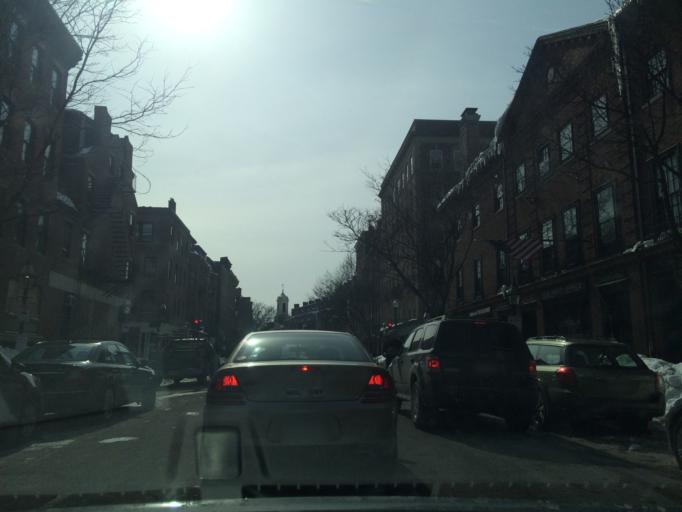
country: US
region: Massachusetts
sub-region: Suffolk County
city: Boston
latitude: 42.3599
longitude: -71.0708
